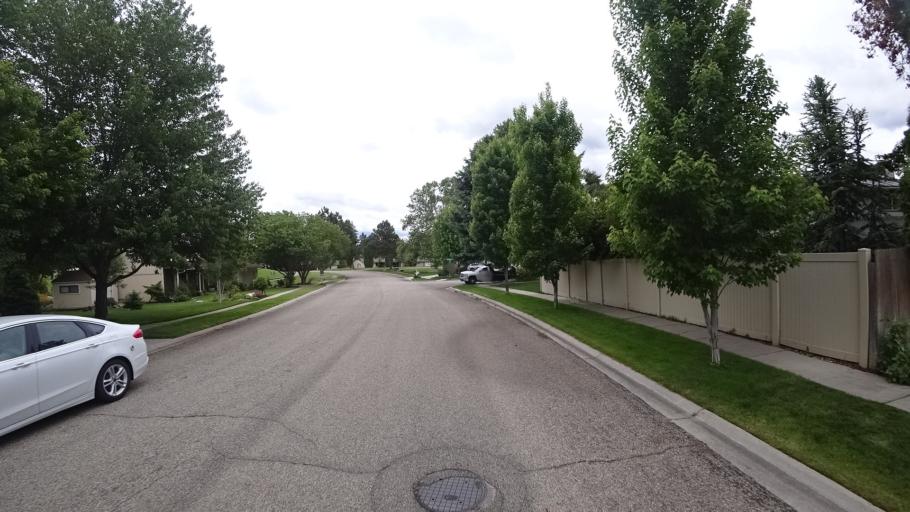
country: US
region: Idaho
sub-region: Ada County
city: Eagle
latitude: 43.6997
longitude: -116.3383
